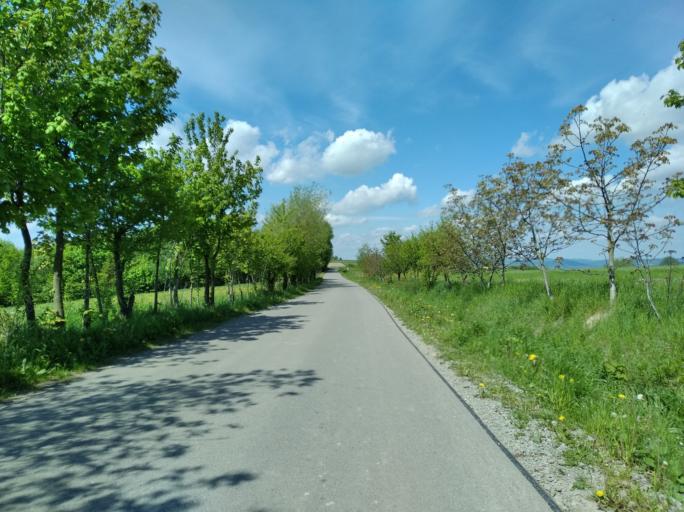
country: PL
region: Subcarpathian Voivodeship
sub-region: Powiat jasielski
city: Kolaczyce
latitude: 49.8392
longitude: 21.4970
